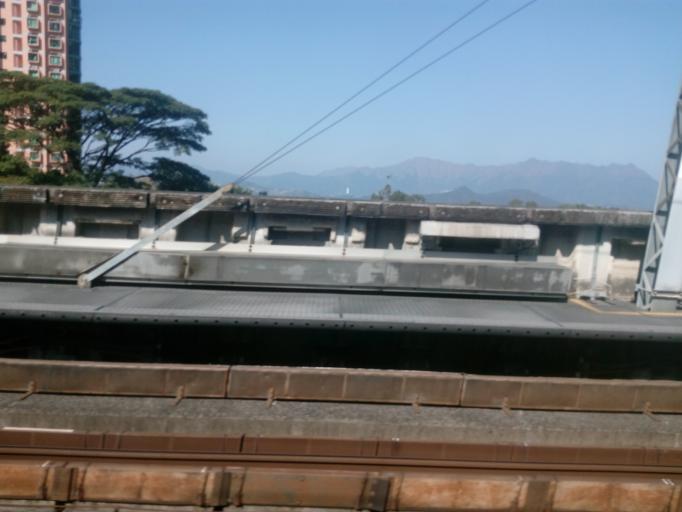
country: HK
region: Sai Kung
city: Sai Kung
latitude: 22.4266
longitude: 114.2391
